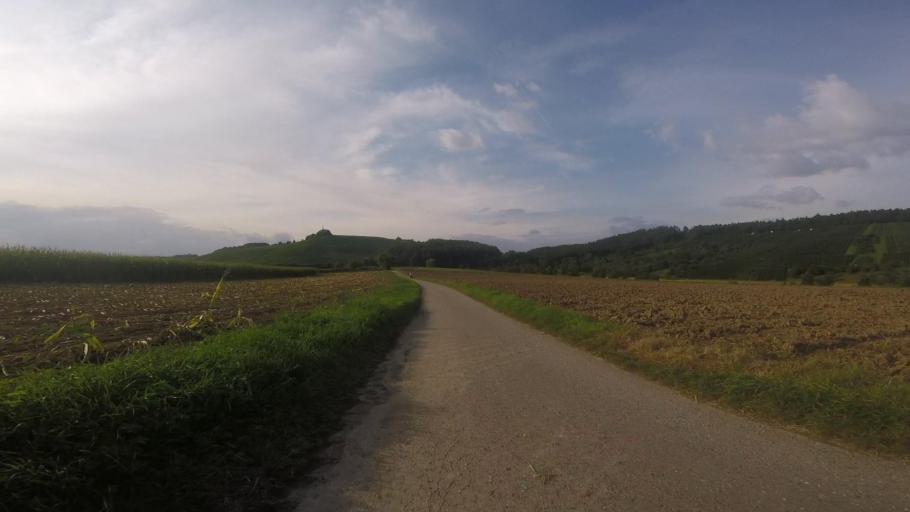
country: DE
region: Baden-Wuerttemberg
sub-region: Regierungsbezirk Stuttgart
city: Aspach
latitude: 48.9933
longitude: 9.3838
